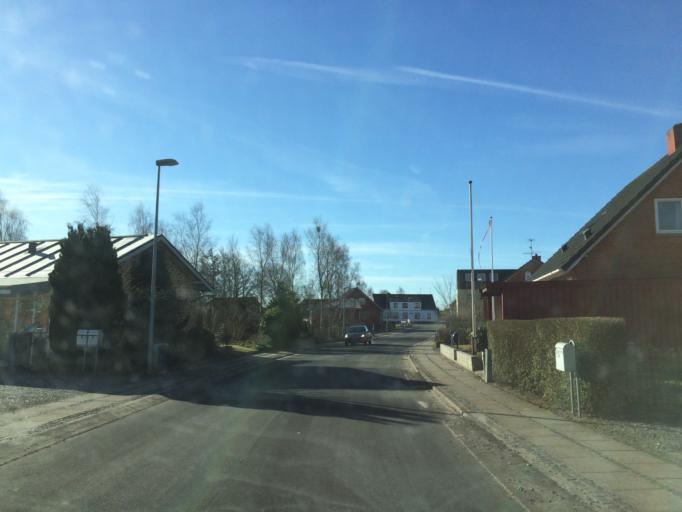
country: DK
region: North Denmark
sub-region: Mariagerfjord Kommune
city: Hobro
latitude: 56.5911
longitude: 9.6352
